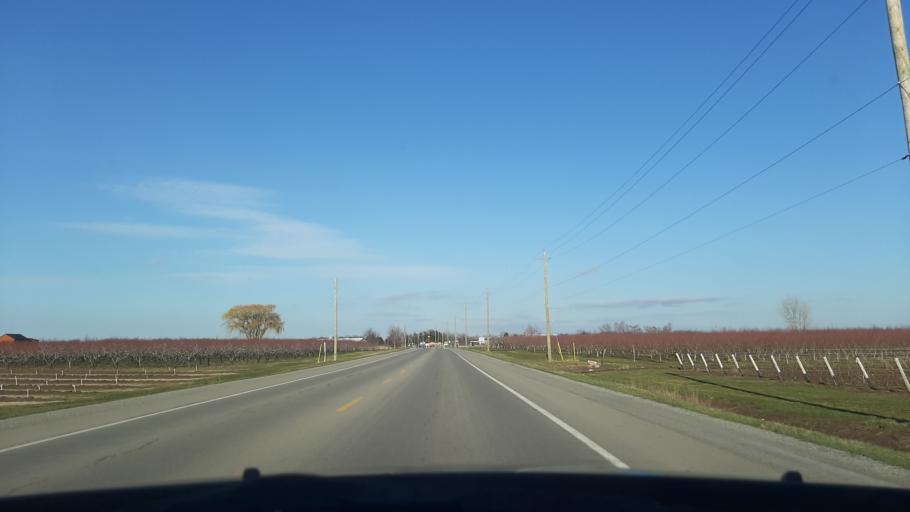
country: CA
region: Ontario
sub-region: Regional Municipality of Niagara
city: St. Catharines
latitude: 43.2199
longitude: -79.1979
